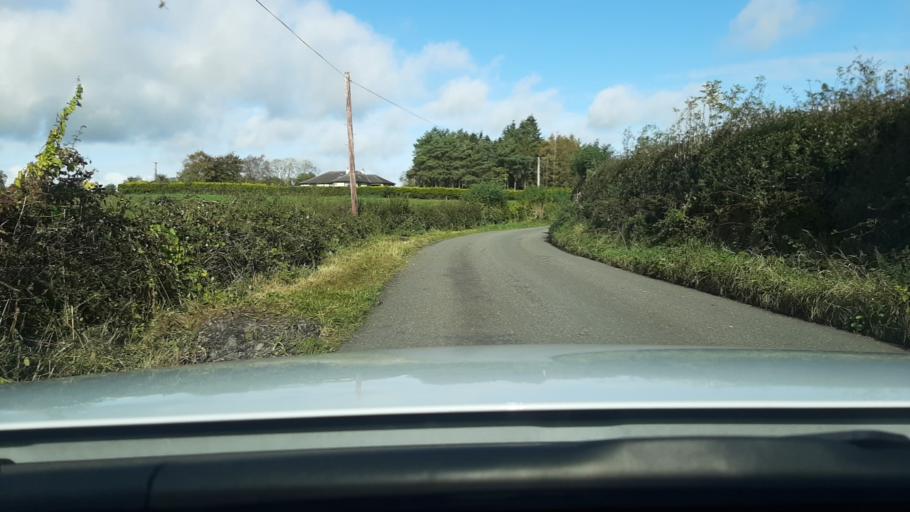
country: IE
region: Leinster
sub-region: Kildare
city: Kildare
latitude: 53.1672
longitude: -6.9188
